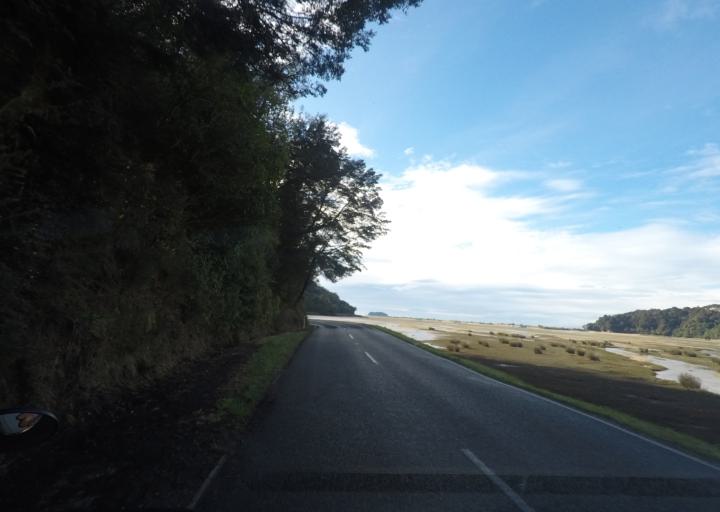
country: NZ
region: Tasman
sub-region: Tasman District
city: Motueka
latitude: -41.0141
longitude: 172.9973
